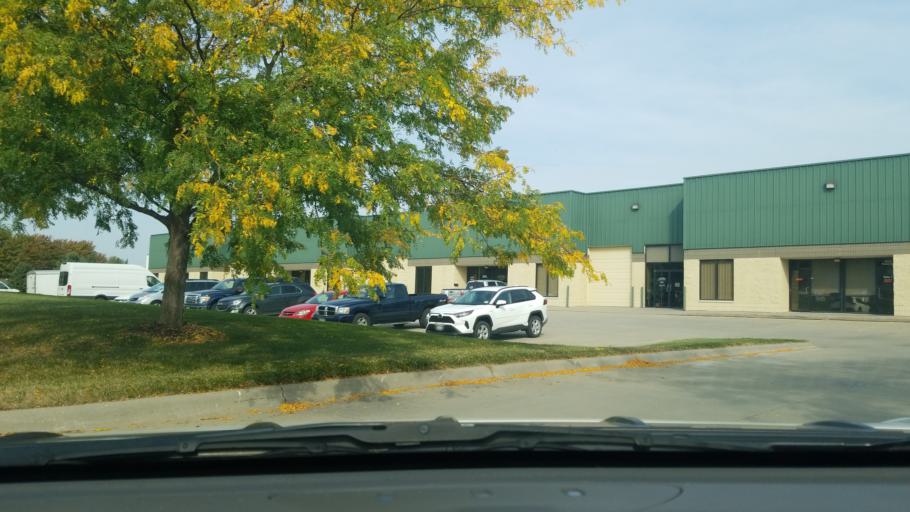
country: US
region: Nebraska
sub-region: Sarpy County
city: Chalco
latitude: 41.1725
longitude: -96.1212
